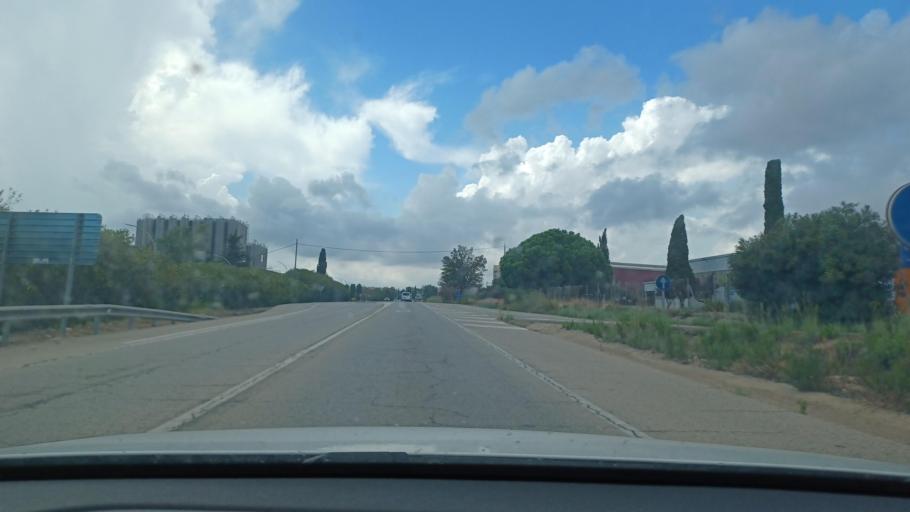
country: ES
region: Catalonia
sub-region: Provincia de Tarragona
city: Vila-seca
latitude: 41.1140
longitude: 1.1658
